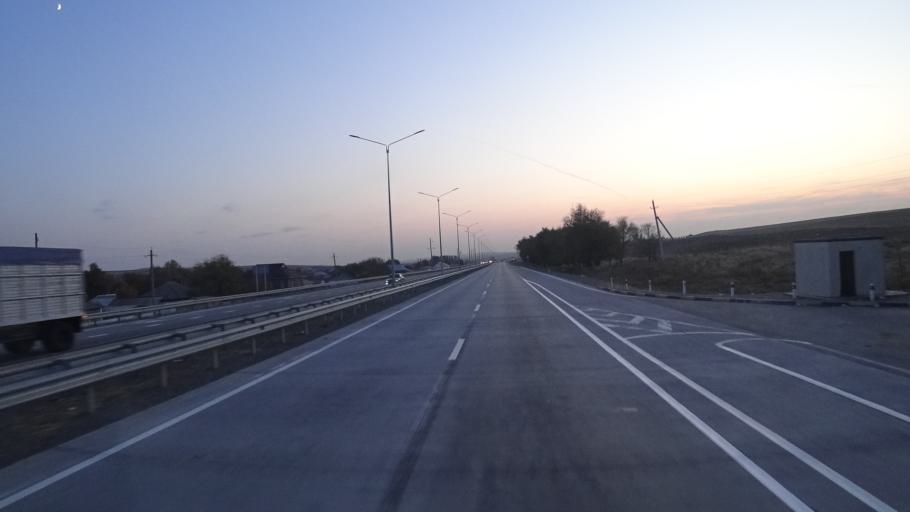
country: KZ
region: Ongtustik Qazaqstan
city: Qazyqurt
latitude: 41.8843
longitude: 69.4405
